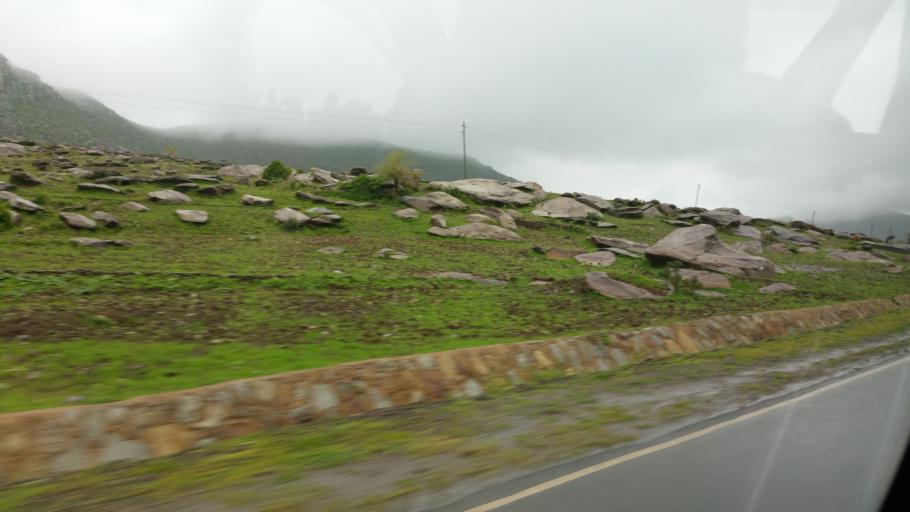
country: ET
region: Tigray
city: Aksum
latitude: 14.1095
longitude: 38.6834
